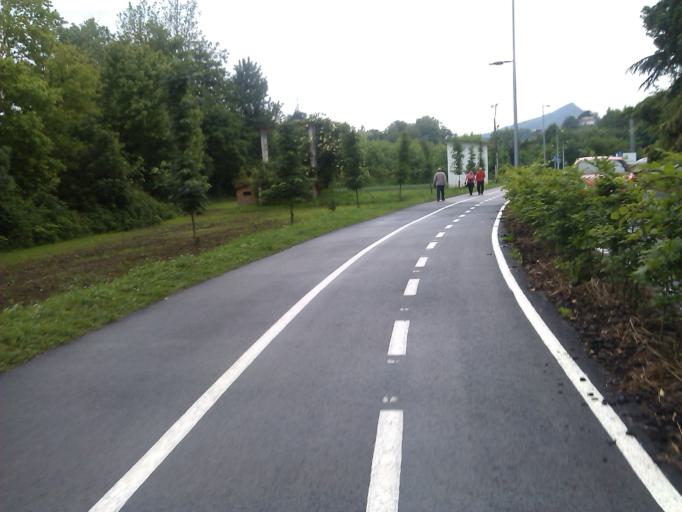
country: ES
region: Basque Country
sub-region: Provincia de Guipuzcoa
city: Hernani
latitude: 43.2647
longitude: -1.9709
